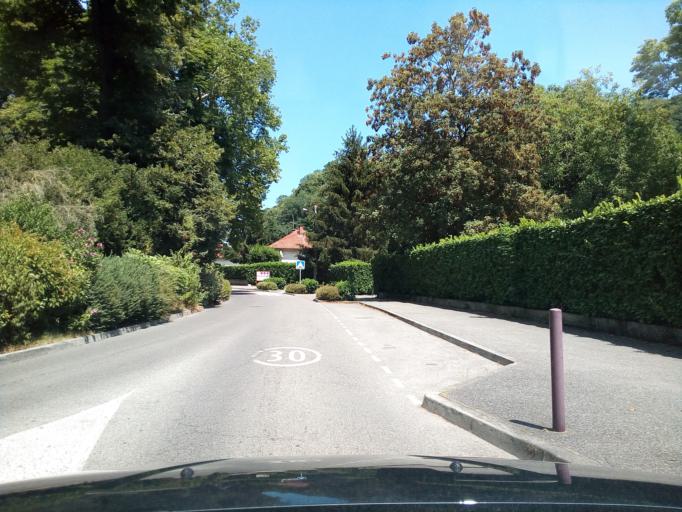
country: FR
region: Rhone-Alpes
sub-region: Departement de l'Isere
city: Le Pont-de-Claix
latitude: 45.1352
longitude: 5.7147
